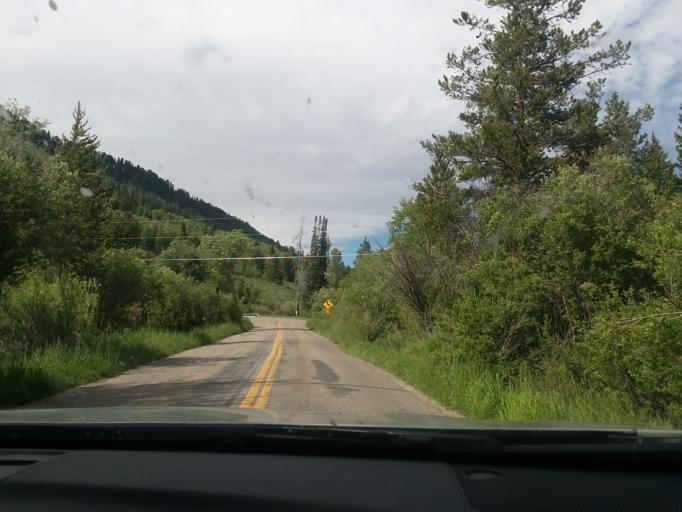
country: US
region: Wyoming
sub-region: Teton County
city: Moose Wilson Road
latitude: 43.5201
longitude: -110.8647
